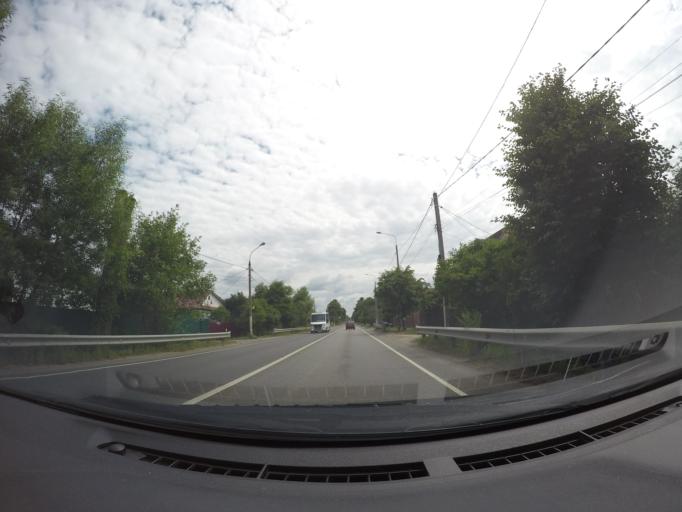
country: RU
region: Moskovskaya
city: Gzhel'
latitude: 55.6226
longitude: 38.3761
